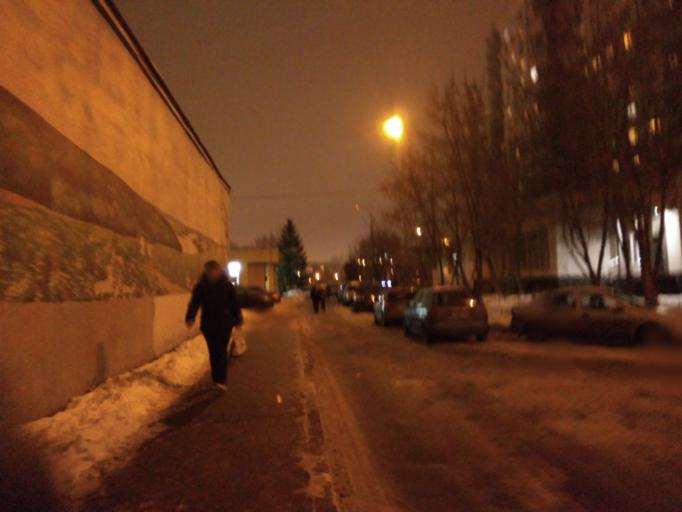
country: RU
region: Moscow
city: Kolomenskoye
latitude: 55.6641
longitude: 37.6489
